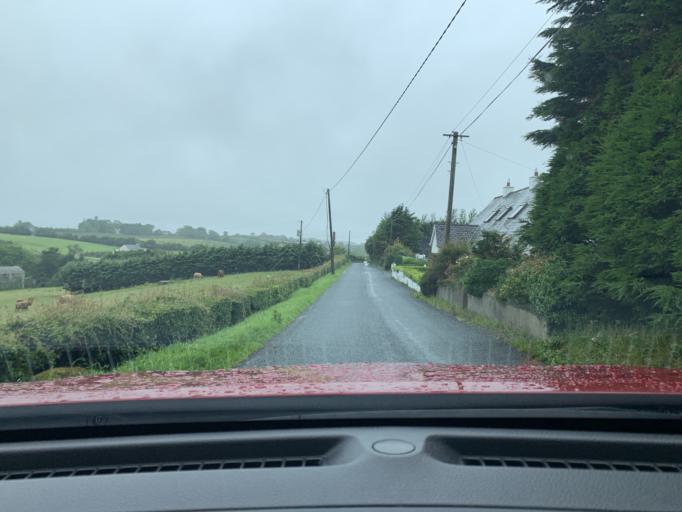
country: IE
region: Connaught
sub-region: Sligo
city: Sligo
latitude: 54.3080
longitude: -8.4712
